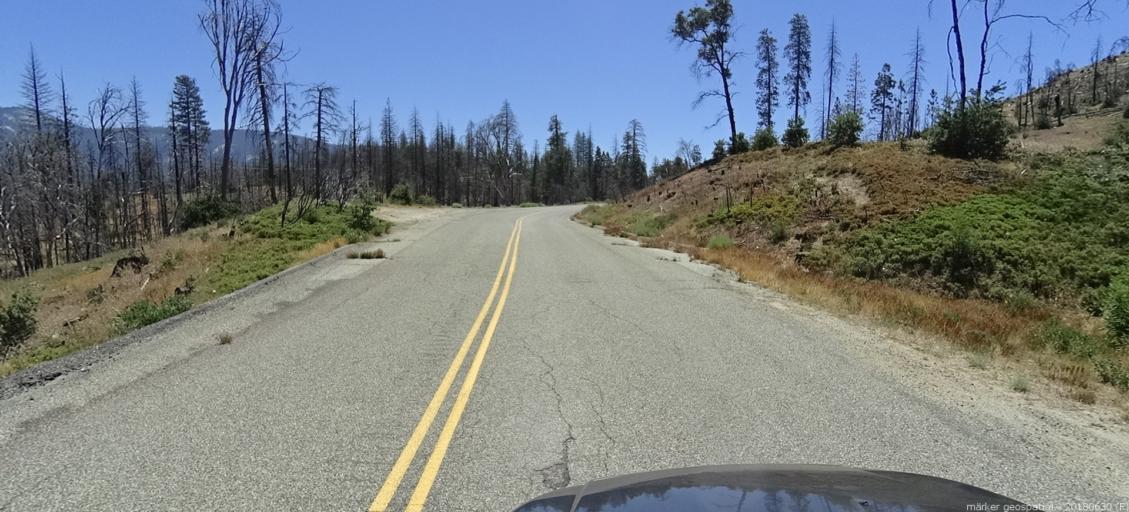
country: US
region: California
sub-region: Fresno County
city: Auberry
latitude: 37.2564
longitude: -119.3524
